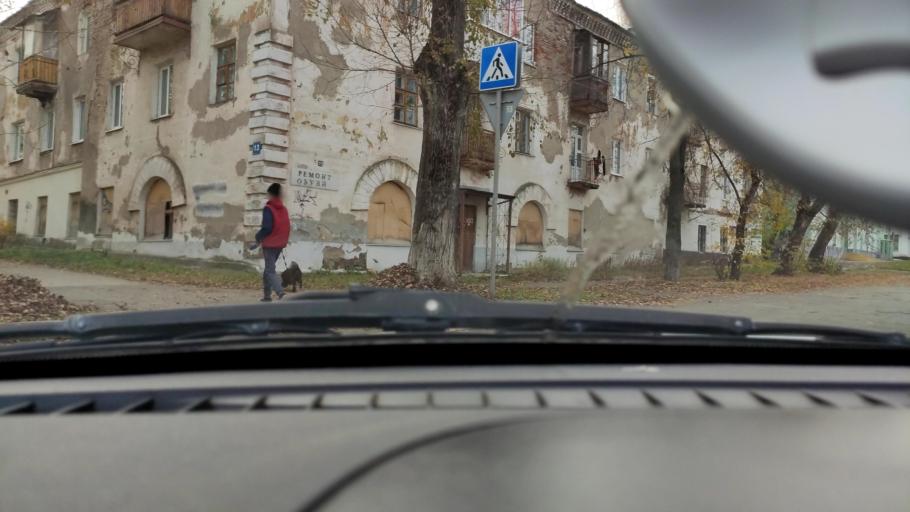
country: RU
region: Perm
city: Polazna
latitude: 58.1271
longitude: 56.3755
